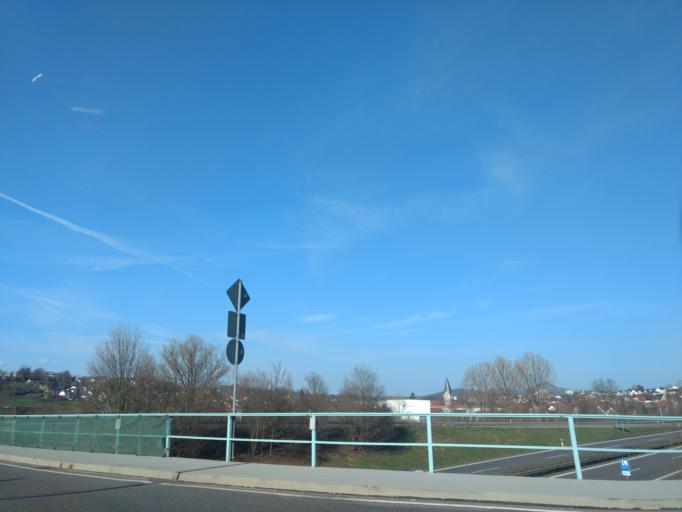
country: DE
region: Baden-Wuerttemberg
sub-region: Regierungsbezirk Stuttgart
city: Uhingen
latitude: 48.7034
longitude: 9.6071
